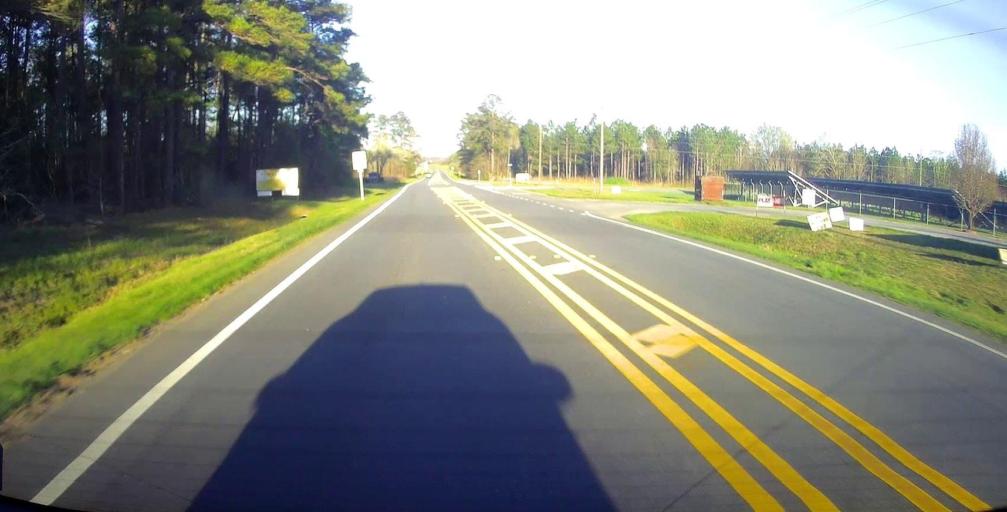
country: US
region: Georgia
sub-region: Wilcox County
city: Abbeville
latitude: 31.9929
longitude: -83.3002
